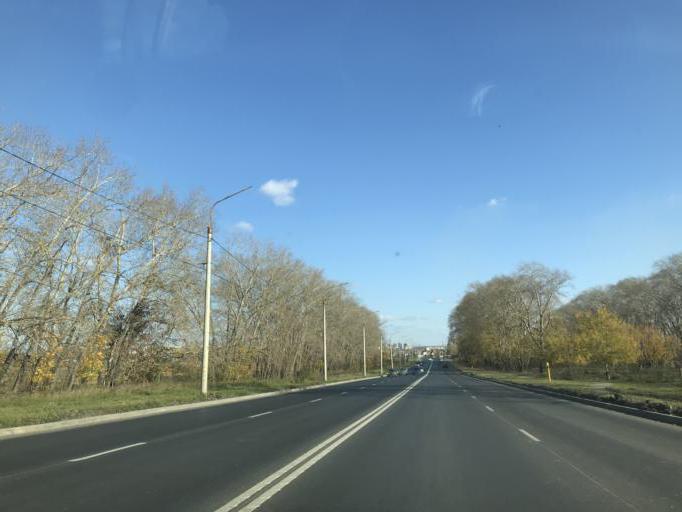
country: RU
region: Chelyabinsk
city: Roshchino
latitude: 55.2402
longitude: 61.3358
